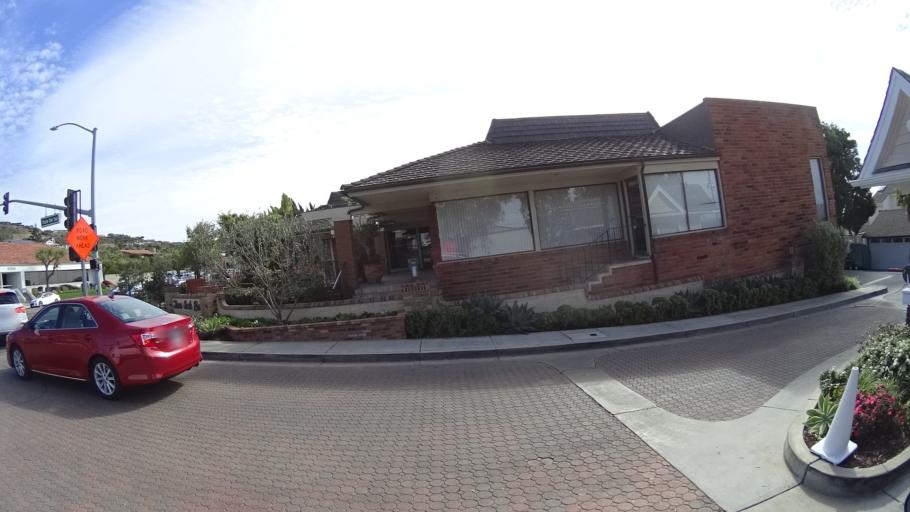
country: US
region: California
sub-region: Orange County
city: Laguna Niguel
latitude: 33.4926
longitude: -117.7351
